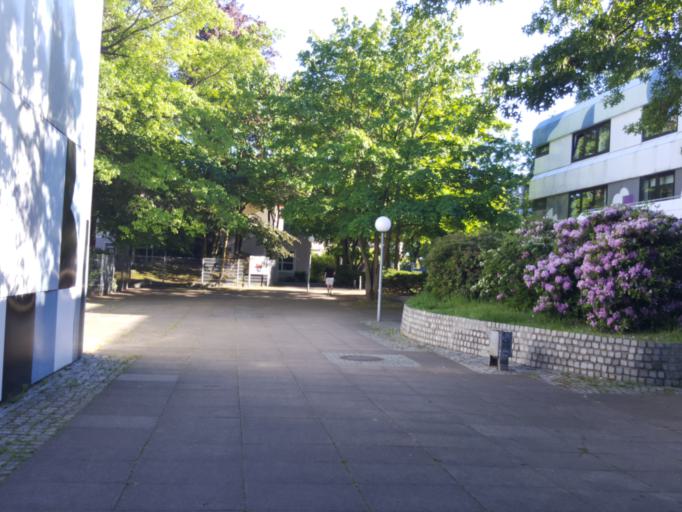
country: DE
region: Schleswig-Holstein
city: Oststeinbek
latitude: 53.5271
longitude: 10.1489
